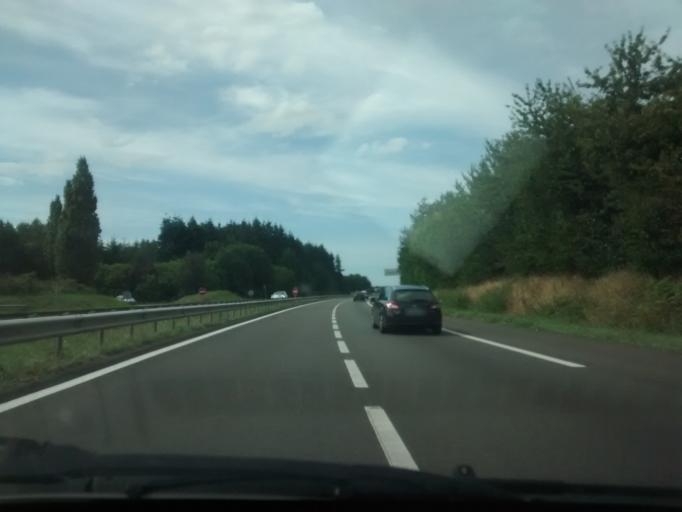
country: FR
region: Brittany
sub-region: Departement d'Ille-et-Vilaine
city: Montauban-de-Bretagne
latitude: 48.1924
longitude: -2.0227
